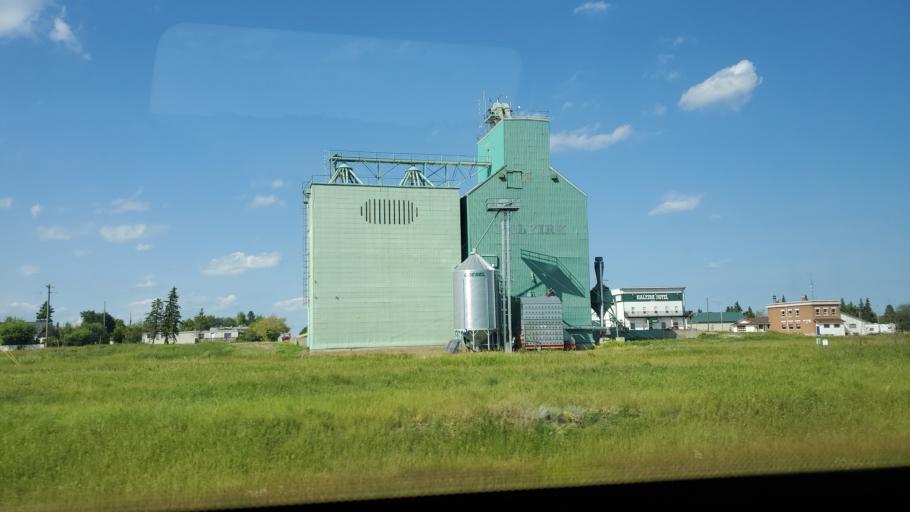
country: CA
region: Alberta
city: Stettler
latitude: 52.2807
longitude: -112.1559
